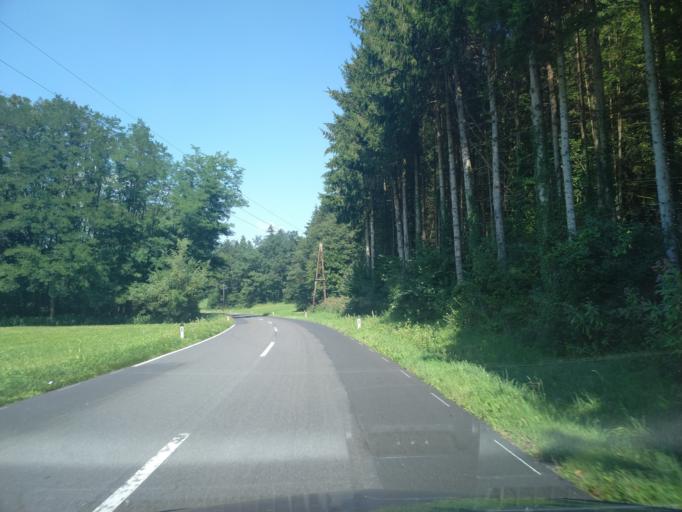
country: AT
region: Styria
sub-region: Politischer Bezirk Leibnitz
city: Leutschach
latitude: 46.7024
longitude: 15.5033
